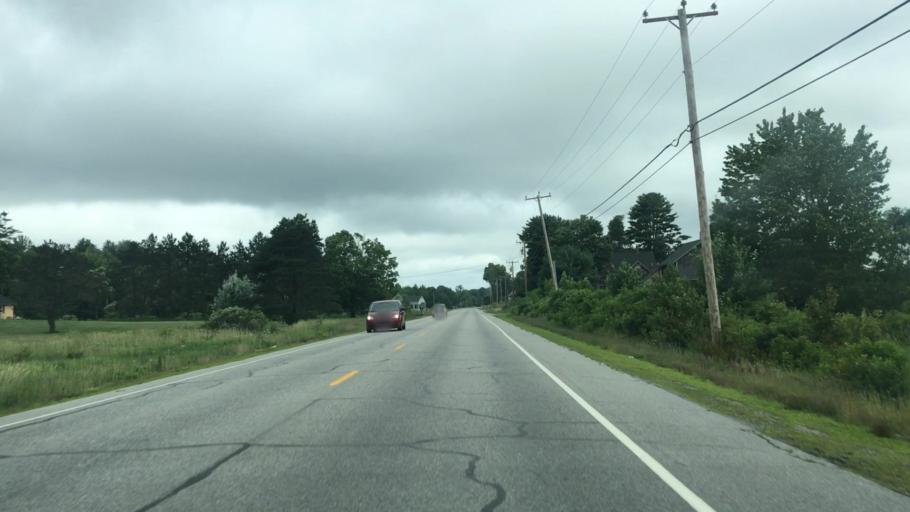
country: US
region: Maine
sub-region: Kennebec County
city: Pittston
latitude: 44.1523
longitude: -69.7441
